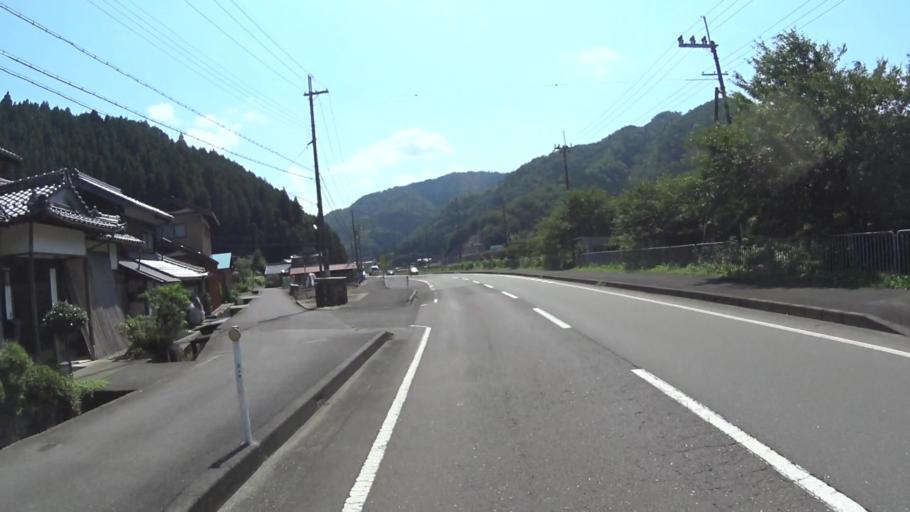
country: JP
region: Fukui
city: Obama
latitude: 35.4211
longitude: 135.6854
